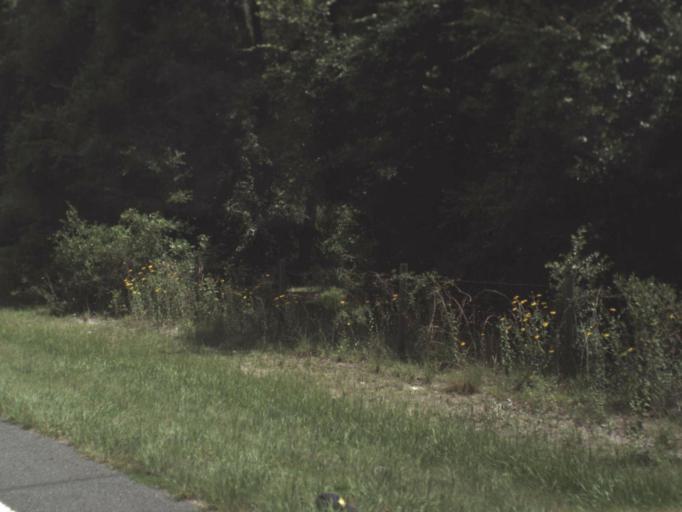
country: US
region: Florida
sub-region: Alachua County
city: Hawthorne
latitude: 29.6708
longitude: -82.0329
